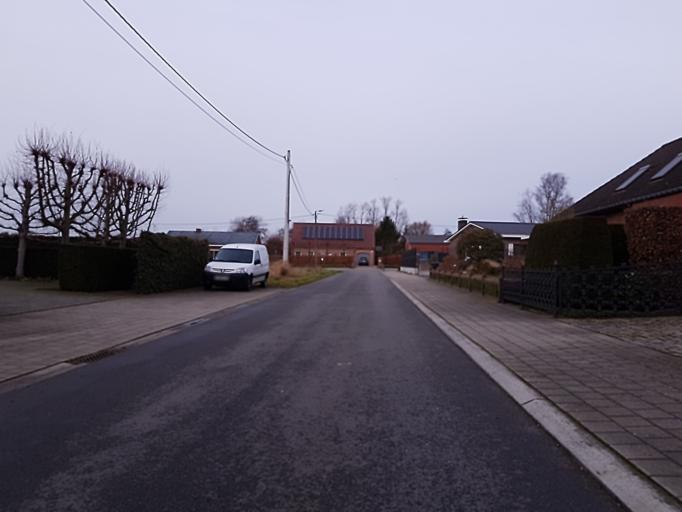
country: BE
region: Flanders
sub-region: Provincie Antwerpen
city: Putte
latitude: 51.0532
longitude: 4.6643
